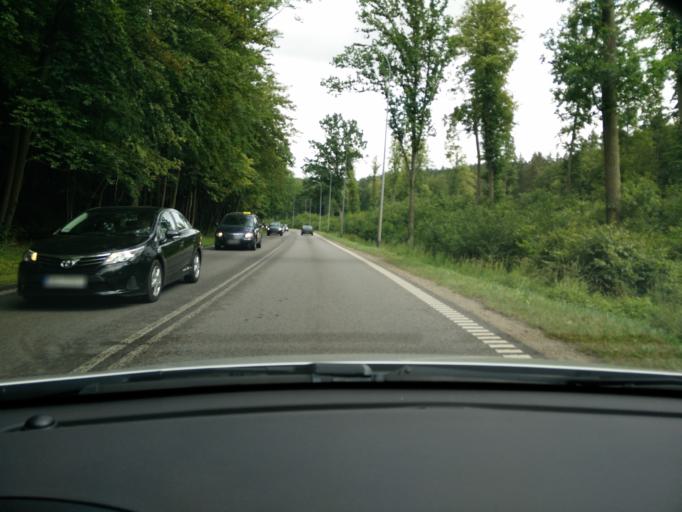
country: PL
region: Pomeranian Voivodeship
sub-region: Gdynia
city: Wielki Kack
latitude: 54.4241
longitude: 18.5039
